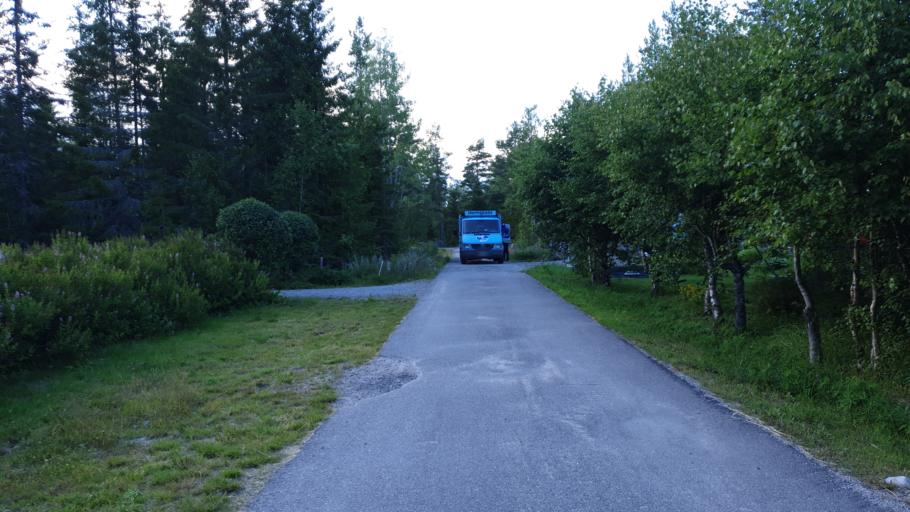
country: SE
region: Gaevleborg
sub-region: Soderhamns Kommun
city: Marielund
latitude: 61.4218
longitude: 17.1549
